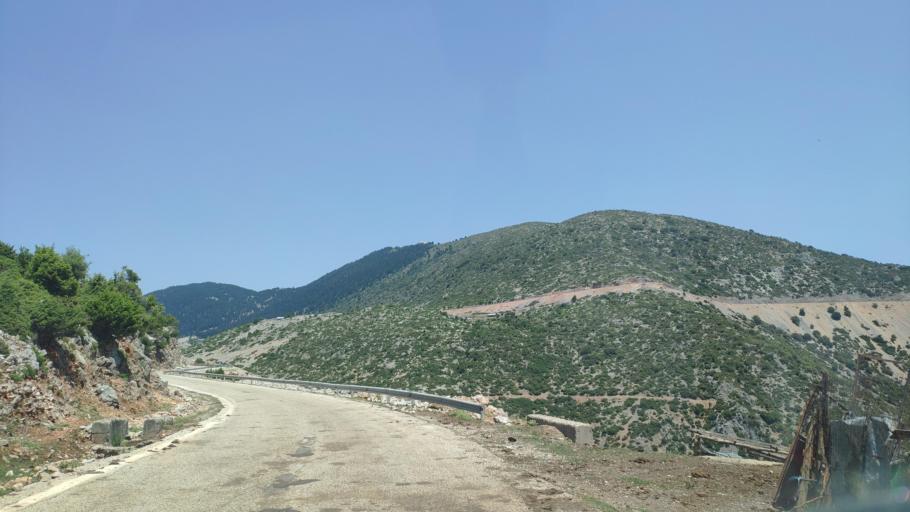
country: GR
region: West Greece
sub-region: Nomos Aitolias kai Akarnanias
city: Krikellos
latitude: 39.0413
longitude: 21.3764
